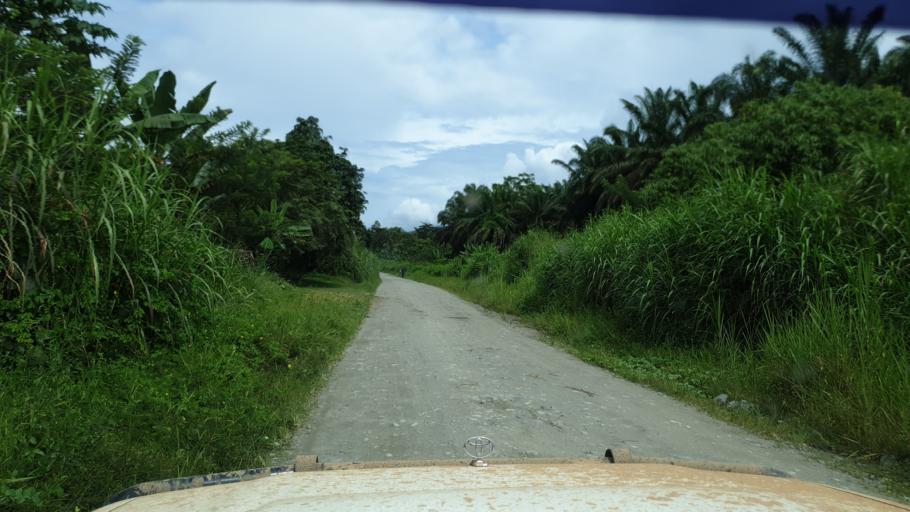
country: PG
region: Northern Province
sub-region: Sohe
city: Kokoda
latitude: -8.8968
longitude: 147.7510
